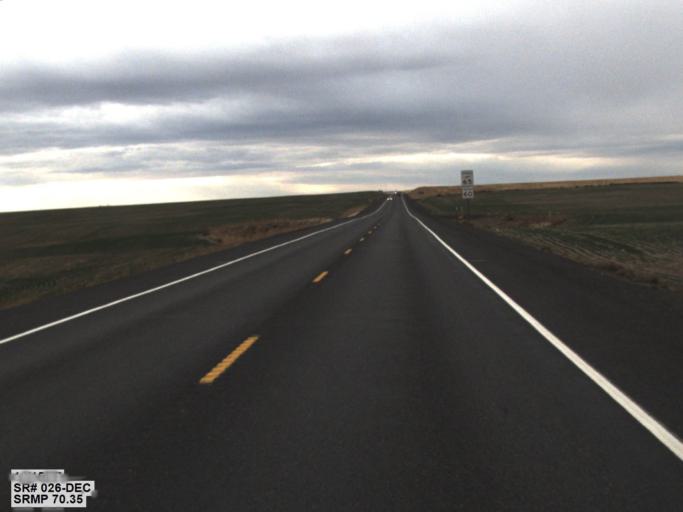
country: US
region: Washington
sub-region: Franklin County
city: Connell
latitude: 46.7948
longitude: -118.5524
